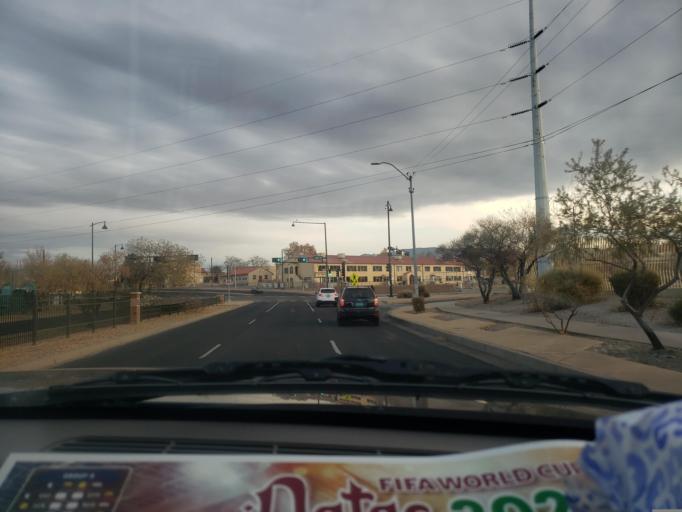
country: US
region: New Mexico
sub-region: Bernalillo County
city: Albuquerque
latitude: 35.0751
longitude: -106.6277
